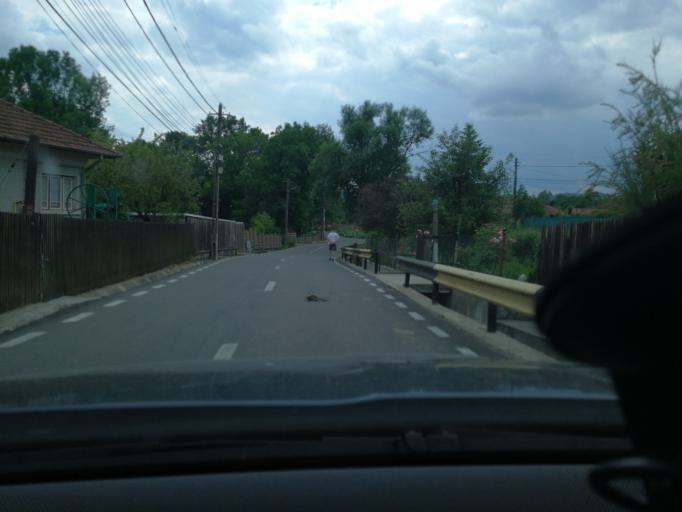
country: RO
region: Prahova
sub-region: Comuna Cornu
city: Cornu de Jos
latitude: 45.1560
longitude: 25.7120
